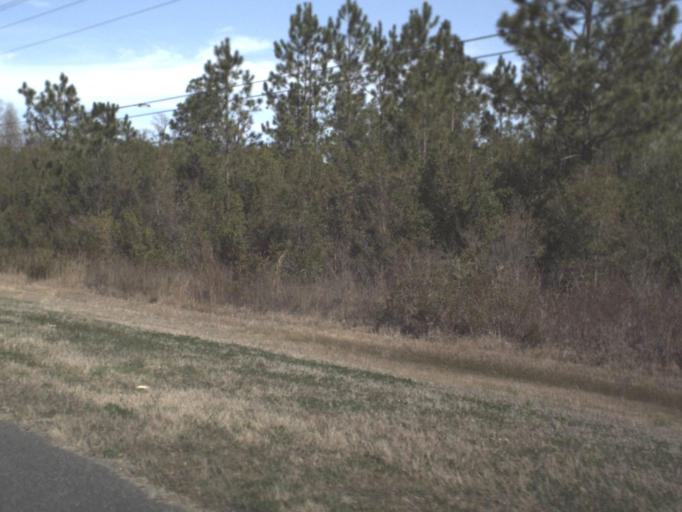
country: US
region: Florida
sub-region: Bay County
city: Lynn Haven
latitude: 30.3557
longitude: -85.6671
